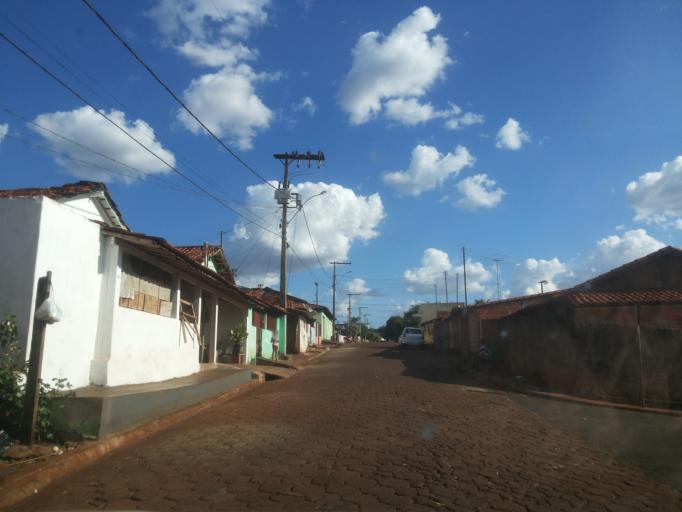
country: BR
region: Minas Gerais
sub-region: Capinopolis
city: Capinopolis
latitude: -18.6839
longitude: -49.5758
